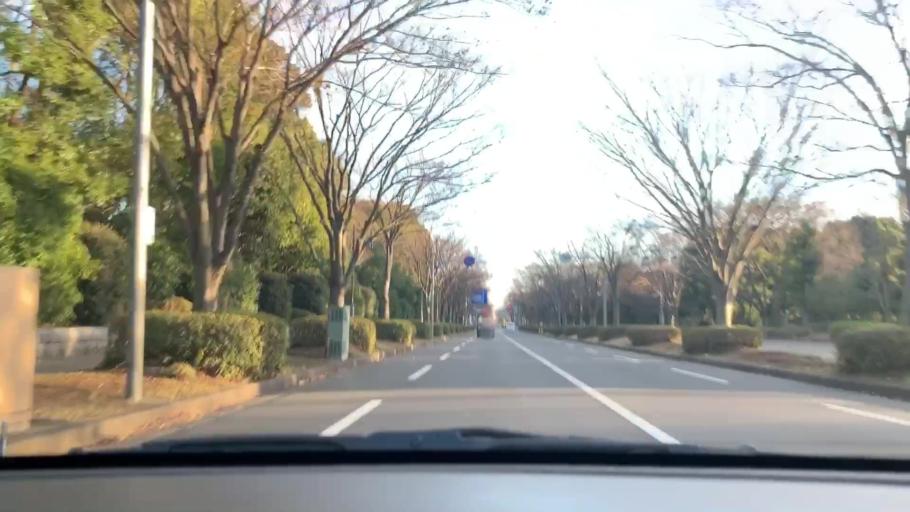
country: JP
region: Chiba
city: Kashiwa
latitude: 35.8979
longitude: 139.9409
